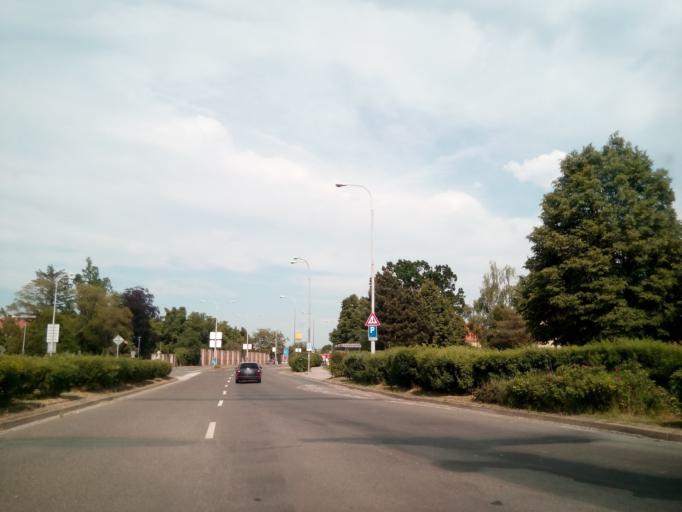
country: CZ
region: South Moravian
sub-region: Mesto Brno
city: Brno
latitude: 49.1760
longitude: 16.6221
